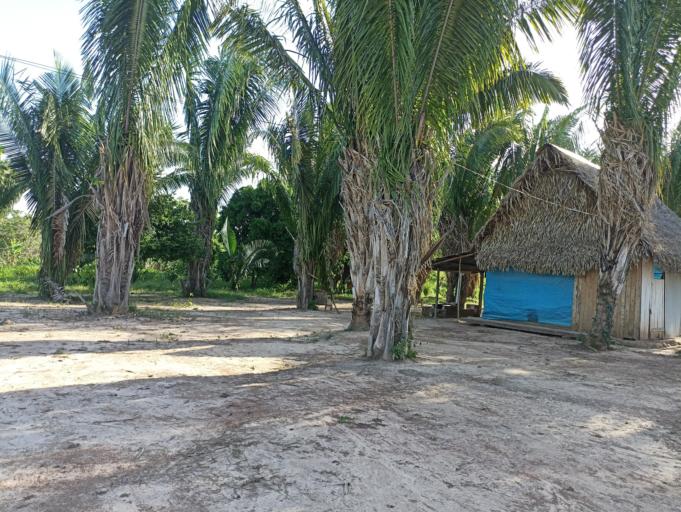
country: PE
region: Ucayali
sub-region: Provincia de Coronel Portillo
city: Puerto Callao
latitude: -8.2756
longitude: -74.6504
